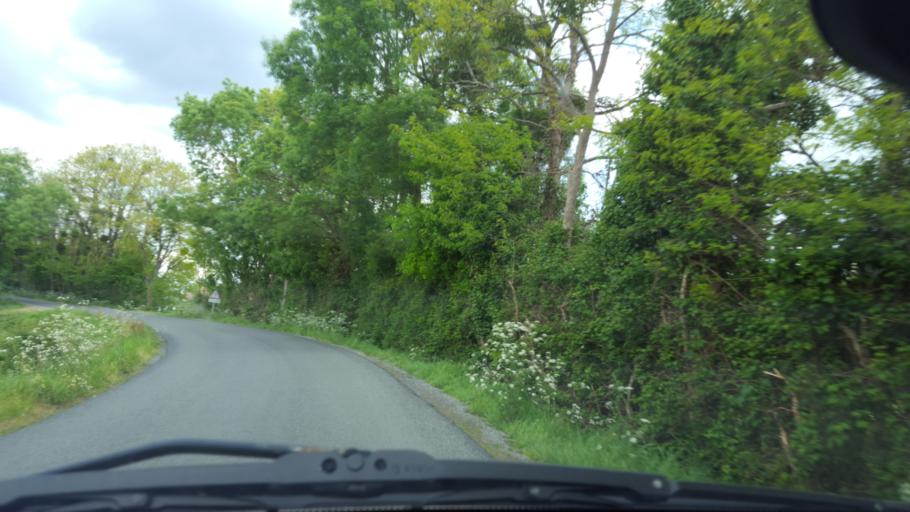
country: FR
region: Pays de la Loire
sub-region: Departement de la Loire-Atlantique
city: Saint-Philbert-de-Grand-Lieu
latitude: 47.0355
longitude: -1.6024
